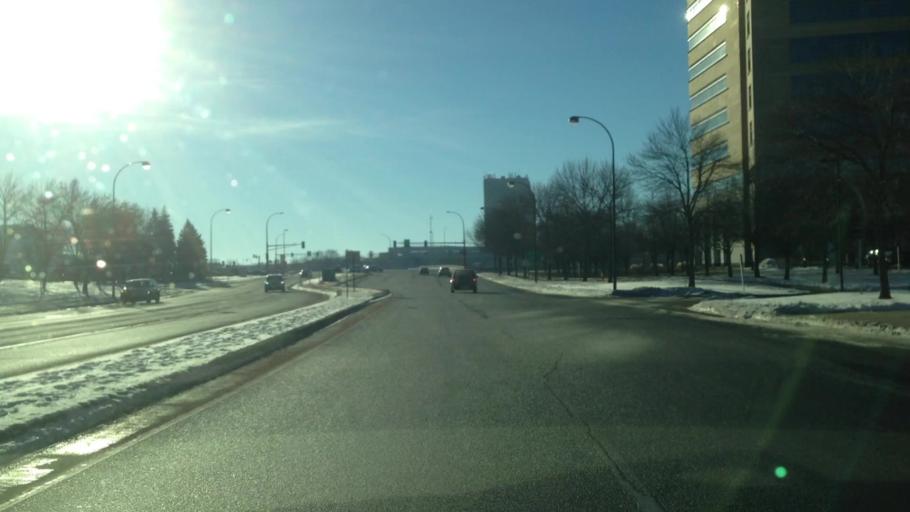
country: US
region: Minnesota
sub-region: Hennepin County
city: Saint Louis Park
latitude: 44.9726
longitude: -93.3521
